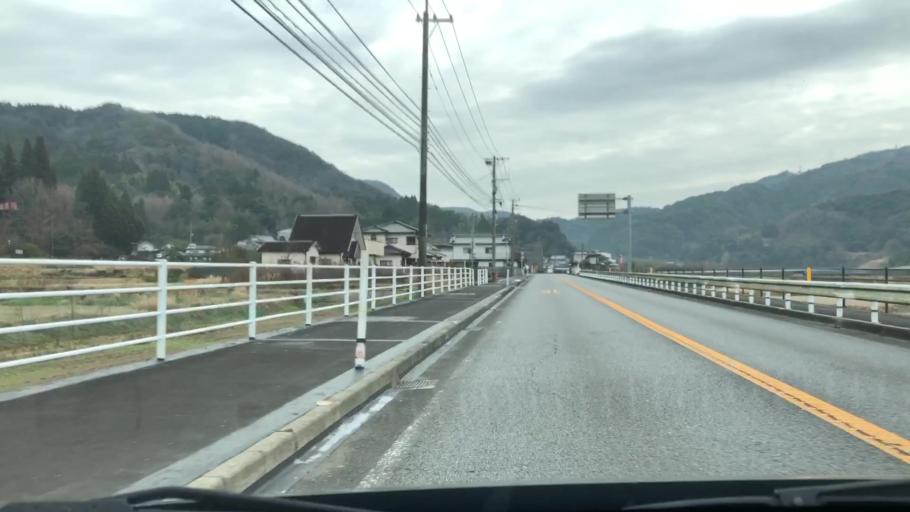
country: JP
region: Oita
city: Usuki
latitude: 33.0061
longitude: 131.7211
